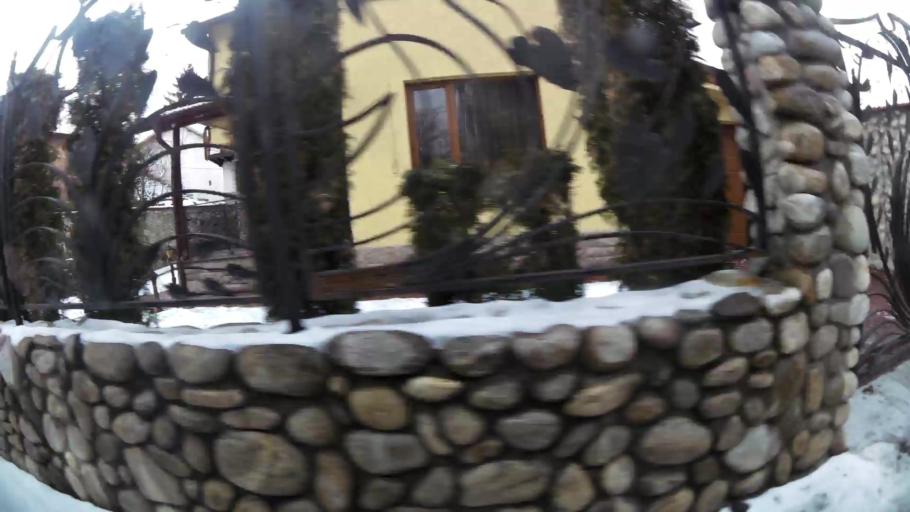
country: BG
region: Sofia-Capital
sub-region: Stolichna Obshtina
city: Sofia
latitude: 42.7281
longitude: 23.3397
